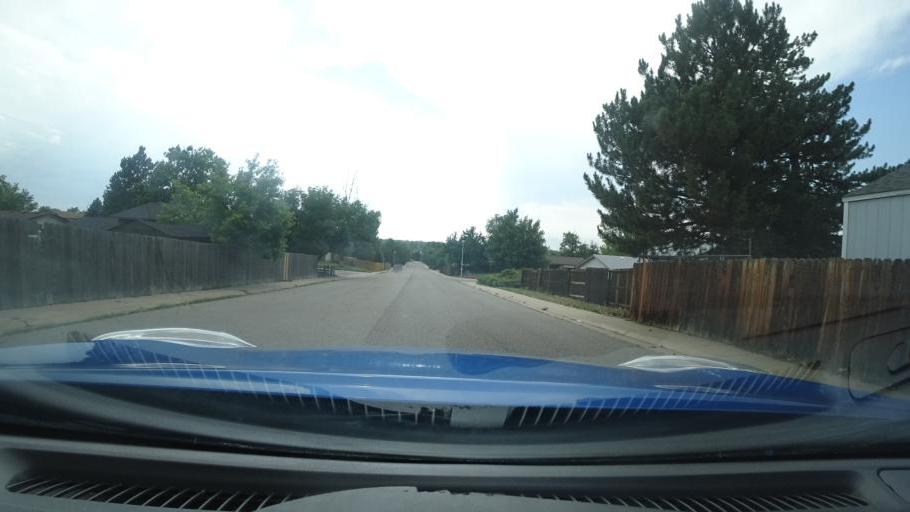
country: US
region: Colorado
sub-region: Adams County
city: Aurora
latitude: 39.6873
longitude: -104.7965
